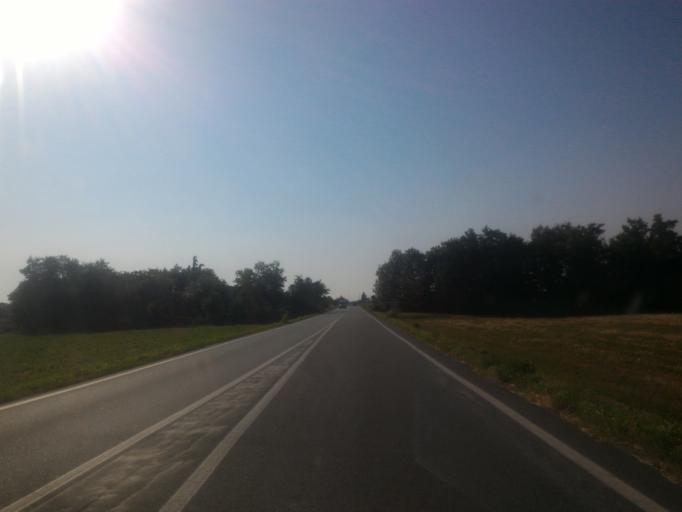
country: IT
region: Piedmont
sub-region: Provincia di Torino
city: Buriasco
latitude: 44.8739
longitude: 7.4028
